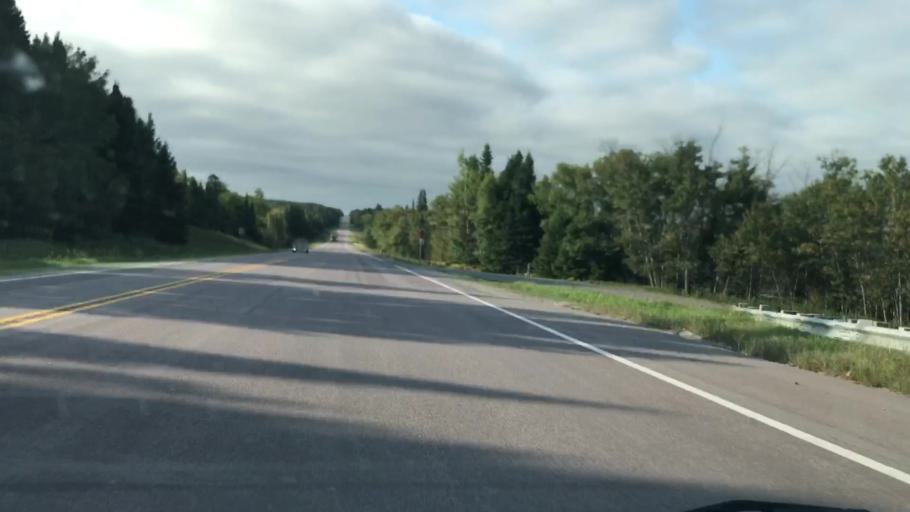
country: US
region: Michigan
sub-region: Luce County
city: Newberry
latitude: 46.3033
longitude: -85.5681
